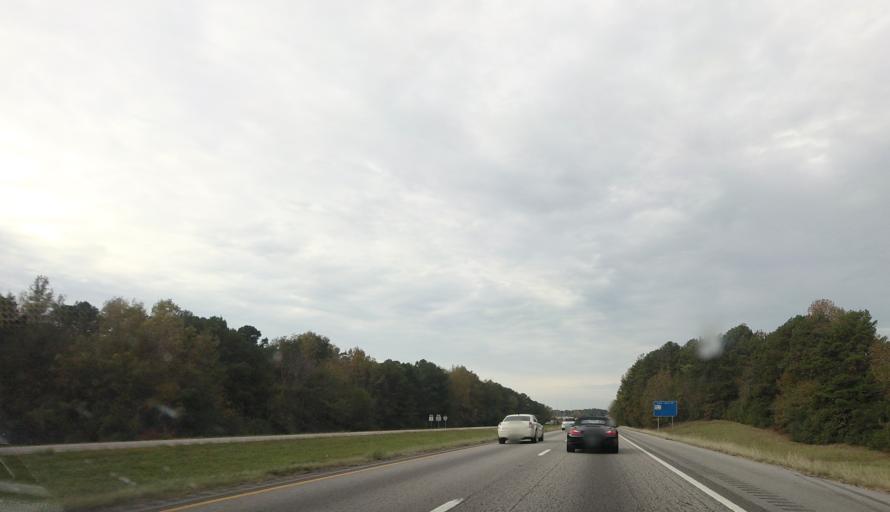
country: US
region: Alabama
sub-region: Lee County
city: Opelika
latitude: 32.6215
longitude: -85.3924
